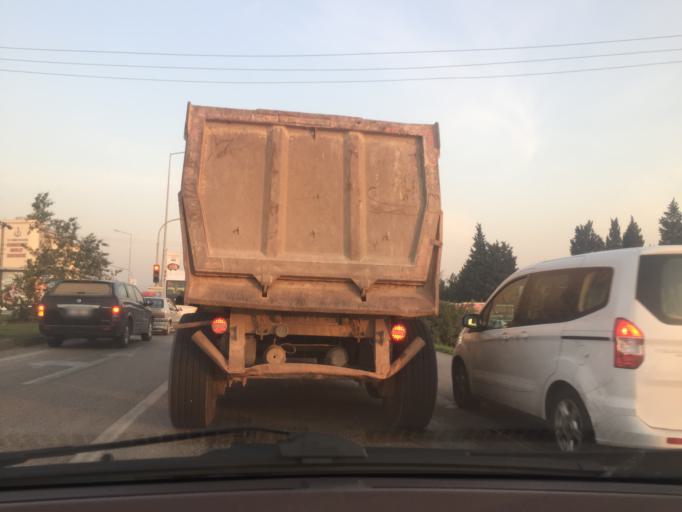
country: TR
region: Bursa
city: Karacabey
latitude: 40.2069
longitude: 28.3498
